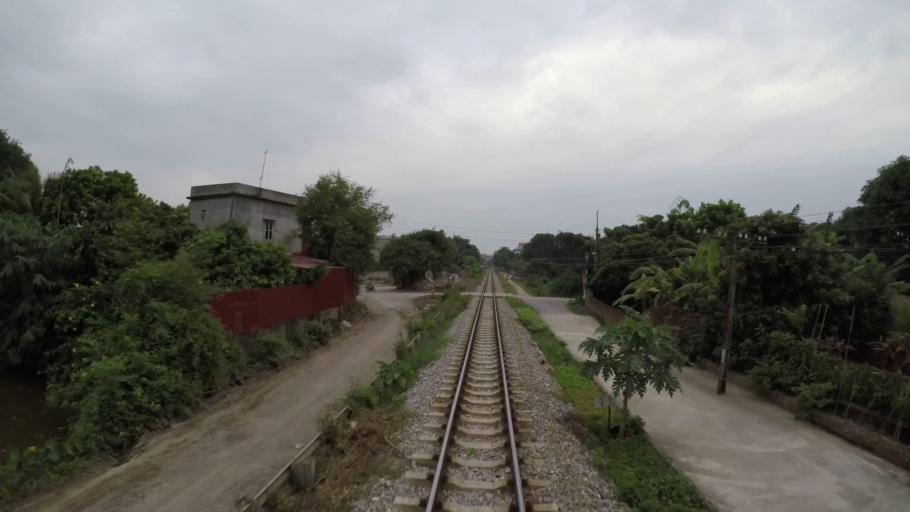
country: VN
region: Hai Duong
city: Ke Sat
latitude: 20.9661
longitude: 106.1397
